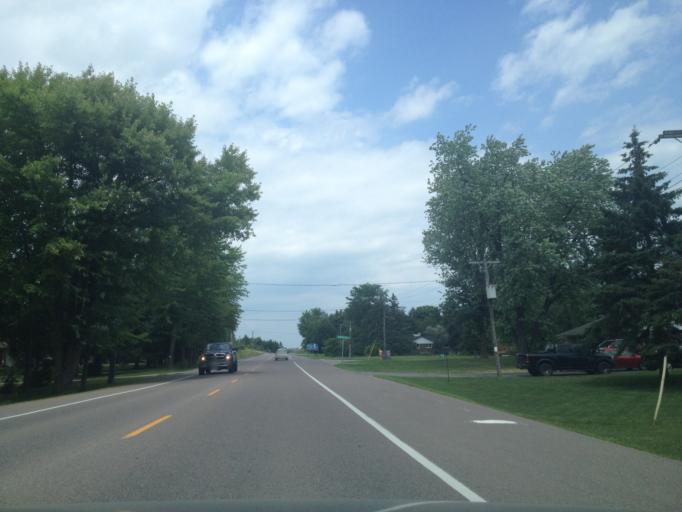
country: CA
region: Ontario
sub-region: Wellington County
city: Guelph
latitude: 43.5784
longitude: -80.2463
